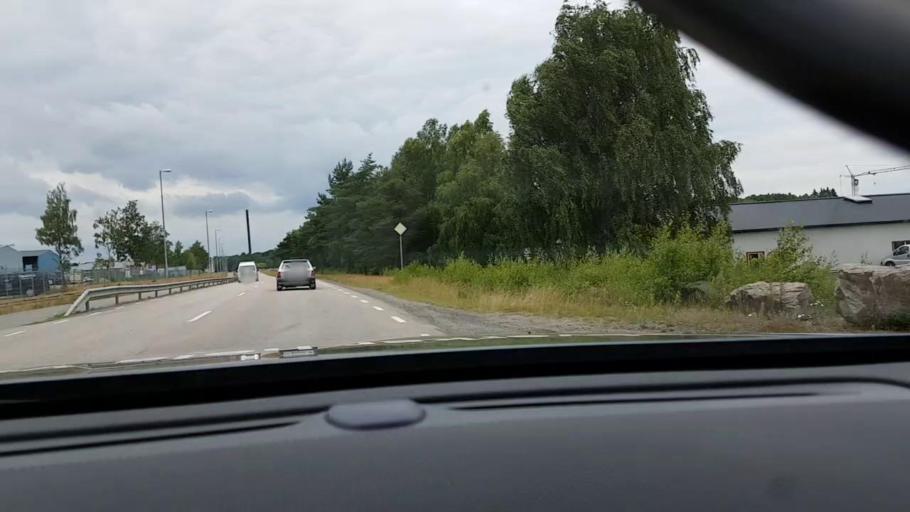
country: SE
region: Skane
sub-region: Hassleholms Kommun
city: Hassleholm
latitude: 56.1571
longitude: 13.8114
